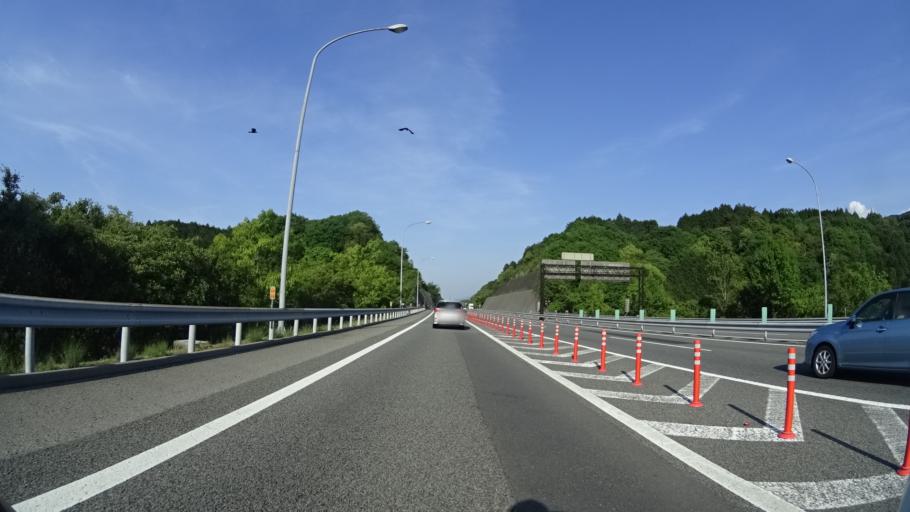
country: JP
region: Ehime
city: Saijo
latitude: 33.8841
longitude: 133.0928
